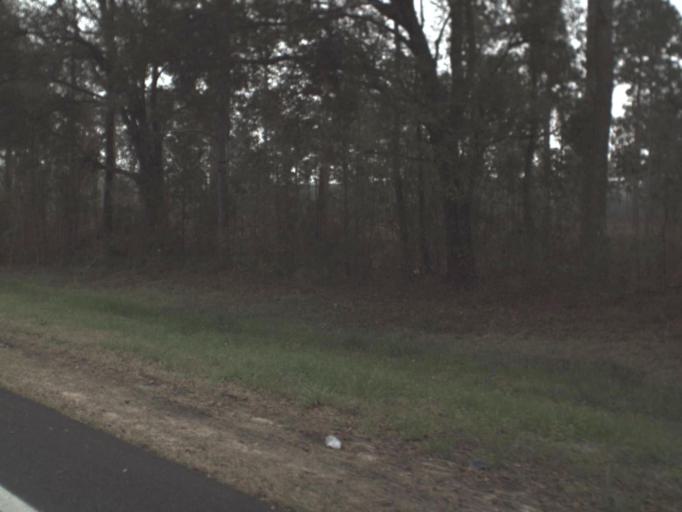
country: US
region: Florida
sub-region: Jefferson County
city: Monticello
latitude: 30.4101
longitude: -83.9084
